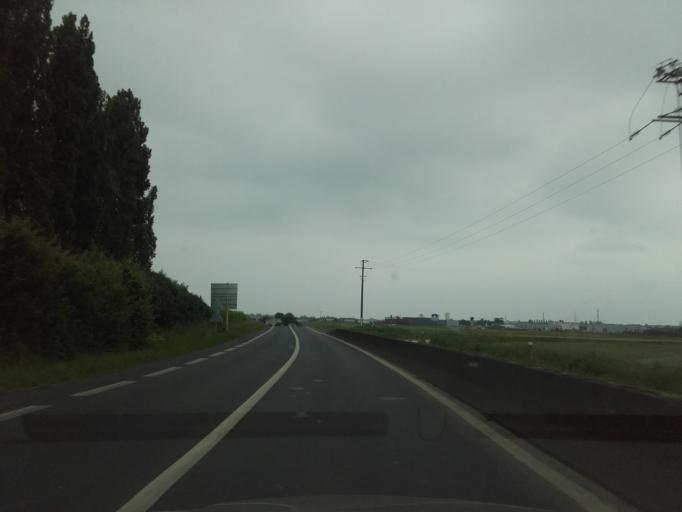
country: FR
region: Centre
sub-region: Departement d'Indre-et-Loire
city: Chanceaux-sur-Choisille
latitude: 47.4482
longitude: 0.6981
